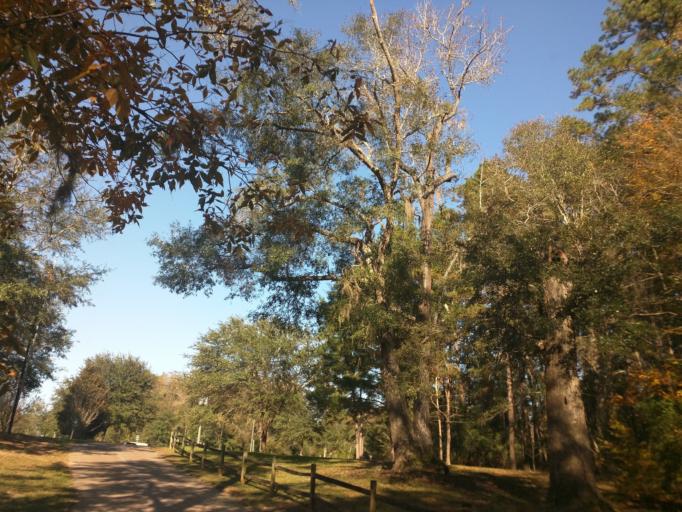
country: US
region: Florida
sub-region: Leon County
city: Tallahassee
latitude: 30.4416
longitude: -84.2130
